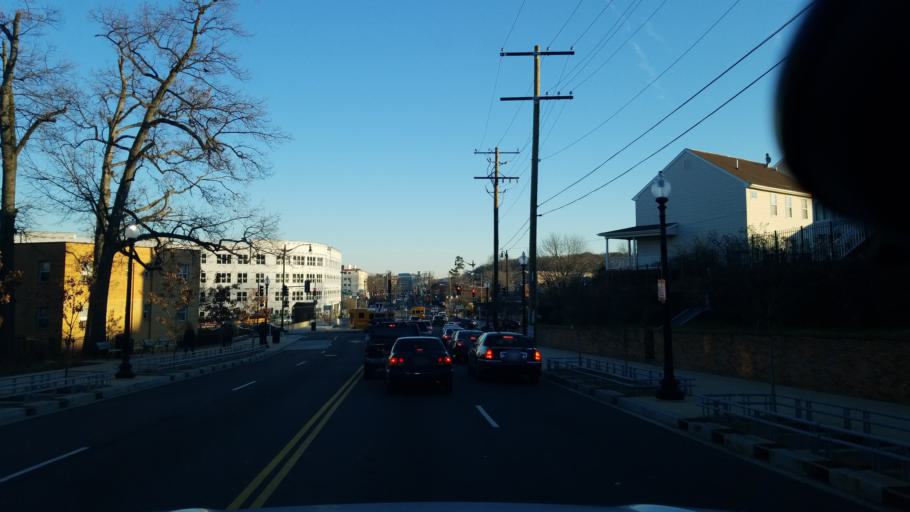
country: US
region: Maryland
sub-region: Prince George's County
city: Coral Hills
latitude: 38.8889
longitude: -76.9537
